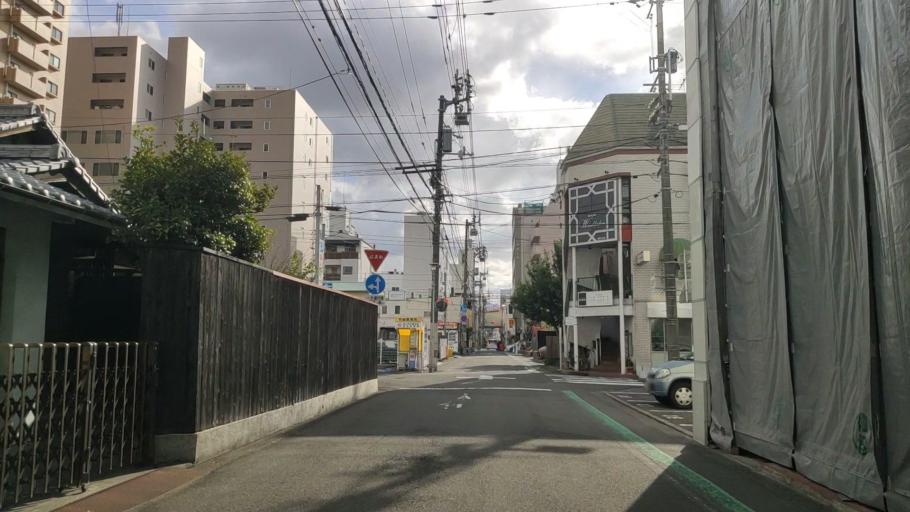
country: JP
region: Ehime
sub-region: Shikoku-chuo Shi
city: Matsuyama
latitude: 33.8380
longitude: 132.7669
